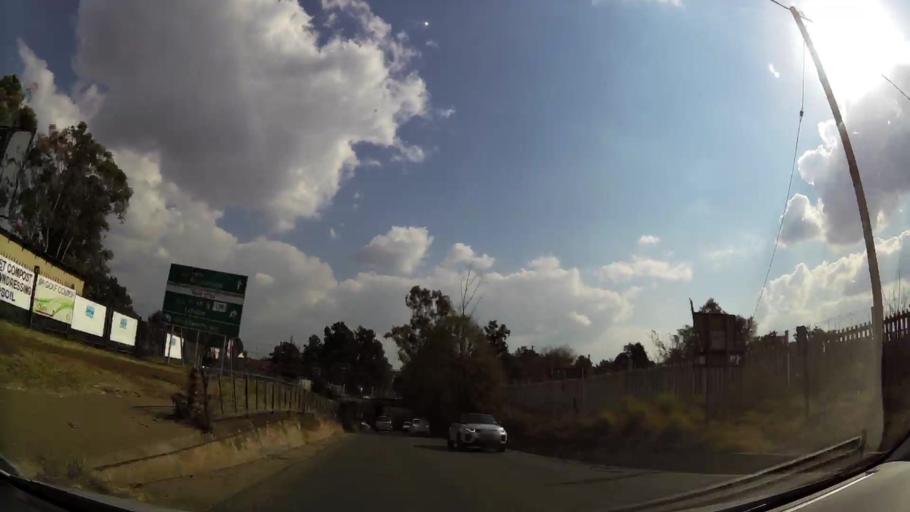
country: ZA
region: Gauteng
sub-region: City of Tshwane Metropolitan Municipality
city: Centurion
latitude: -25.8773
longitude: 28.2252
